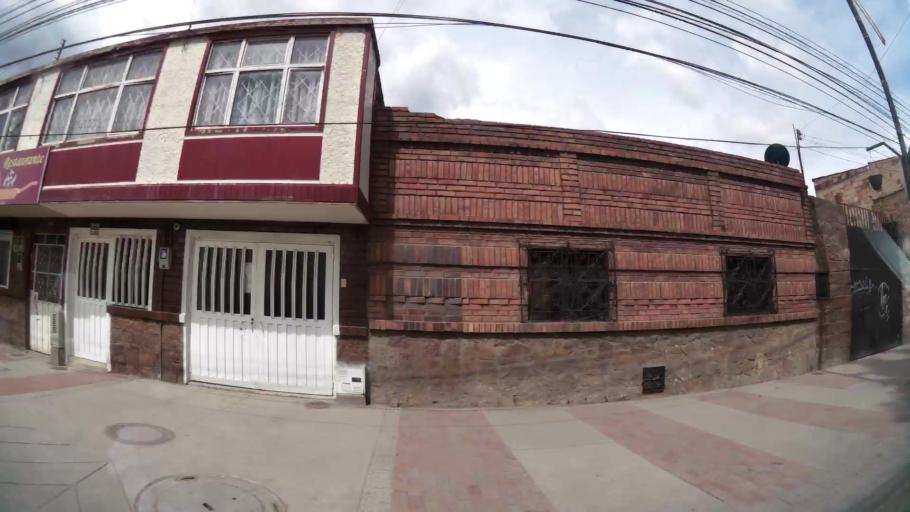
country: CO
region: Cundinamarca
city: Funza
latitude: 4.7038
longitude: -74.2034
